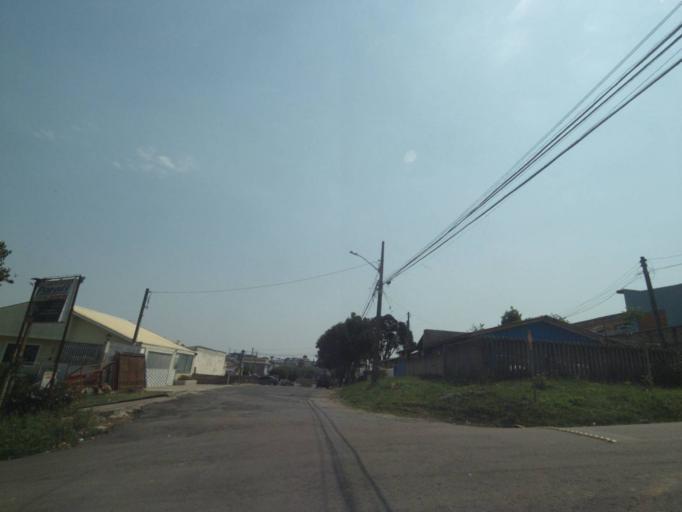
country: BR
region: Parana
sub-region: Sao Jose Dos Pinhais
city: Sao Jose dos Pinhais
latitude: -25.5369
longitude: -49.2489
